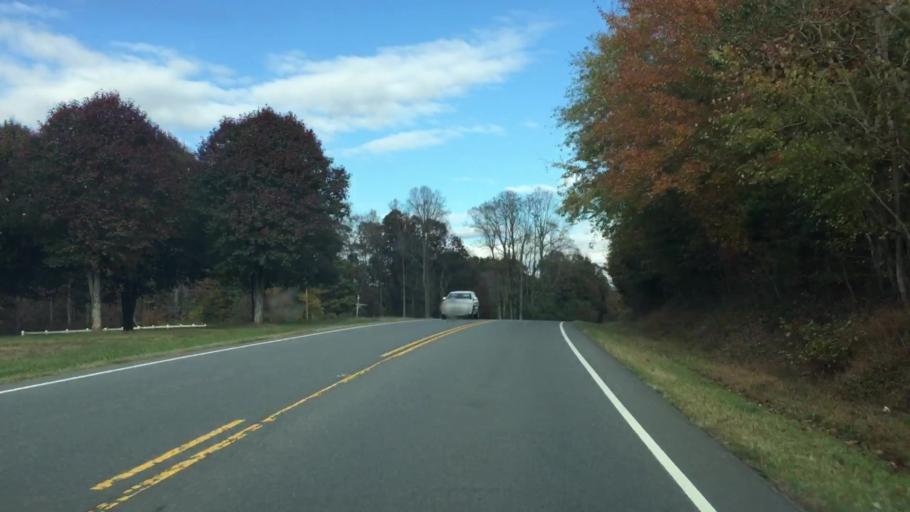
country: US
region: North Carolina
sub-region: Forsyth County
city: Walkertown
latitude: 36.1830
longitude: -80.1174
